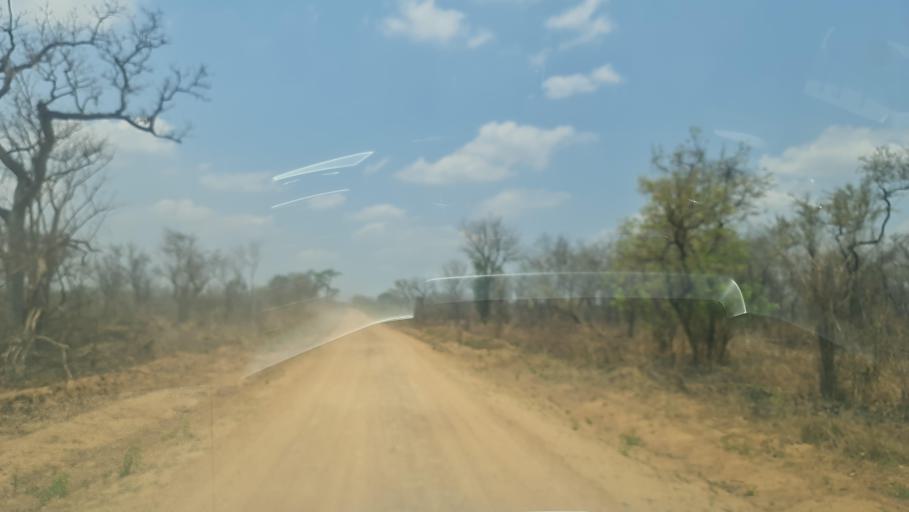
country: MW
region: Southern Region
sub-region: Nsanje District
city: Nsanje
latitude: -17.5700
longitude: 35.9047
